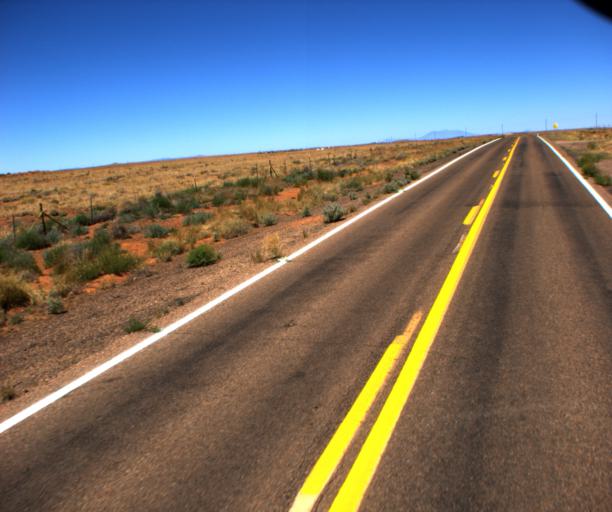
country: US
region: Arizona
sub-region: Navajo County
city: Winslow
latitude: 35.0031
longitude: -110.6869
